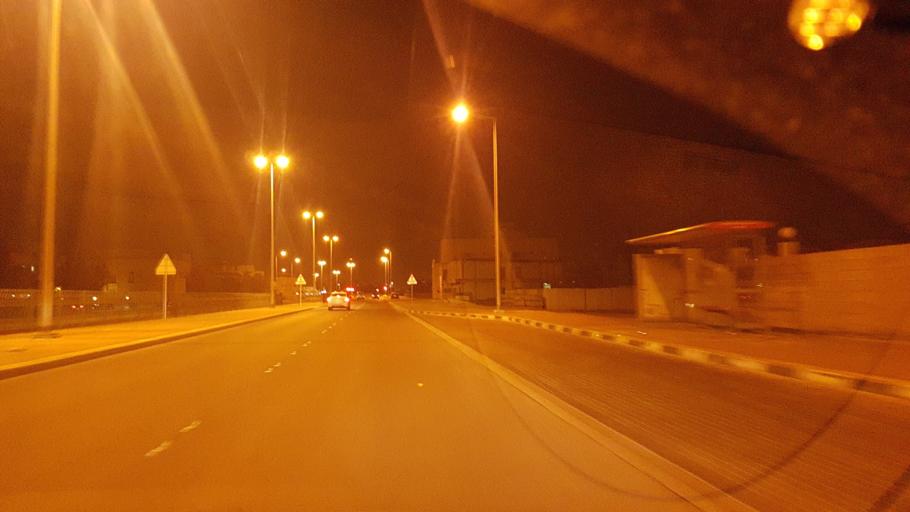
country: BH
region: Muharraq
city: Al Hadd
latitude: 26.2513
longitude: 50.6511
